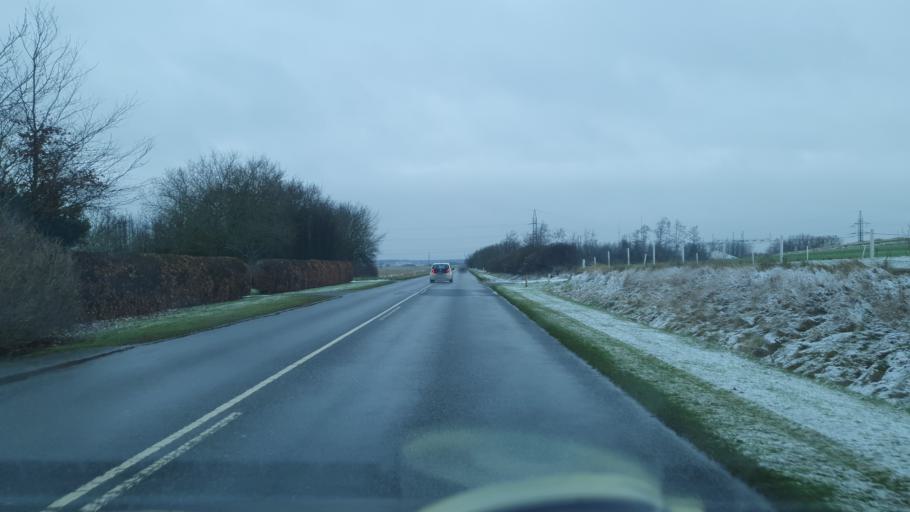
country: DK
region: North Denmark
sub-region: Jammerbugt Kommune
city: Brovst
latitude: 57.1114
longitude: 9.5007
